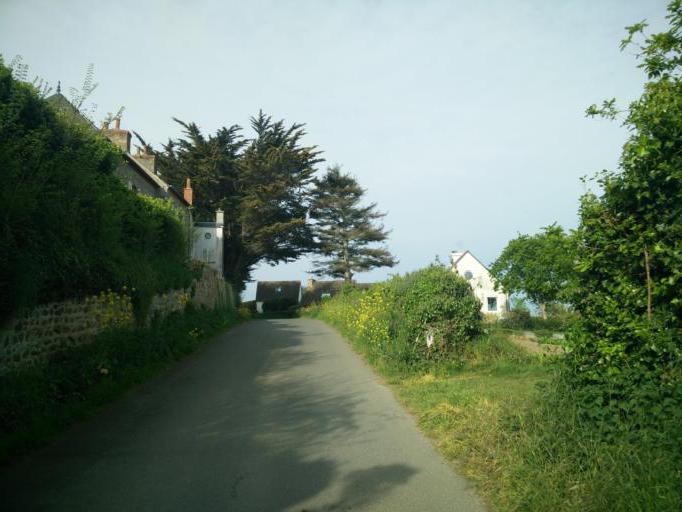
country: FR
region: Brittany
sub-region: Departement des Cotes-d'Armor
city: Lezardrieux
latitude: 48.8284
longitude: -3.0868
